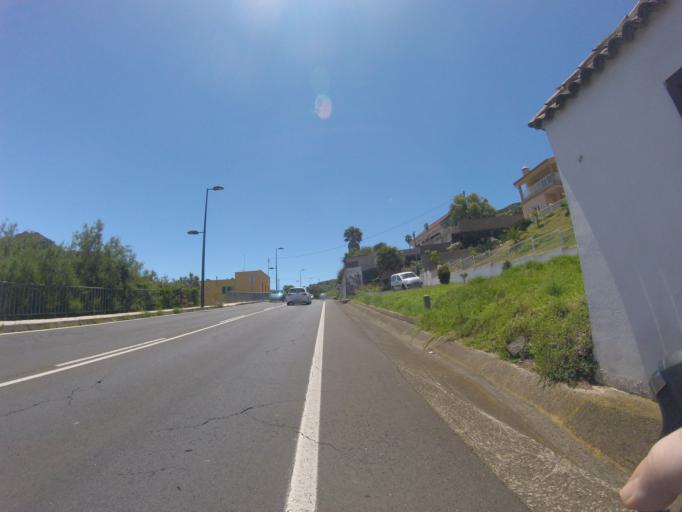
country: ES
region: Canary Islands
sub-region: Provincia de Santa Cruz de Tenerife
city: Tegueste
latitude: 28.5153
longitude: -16.3168
